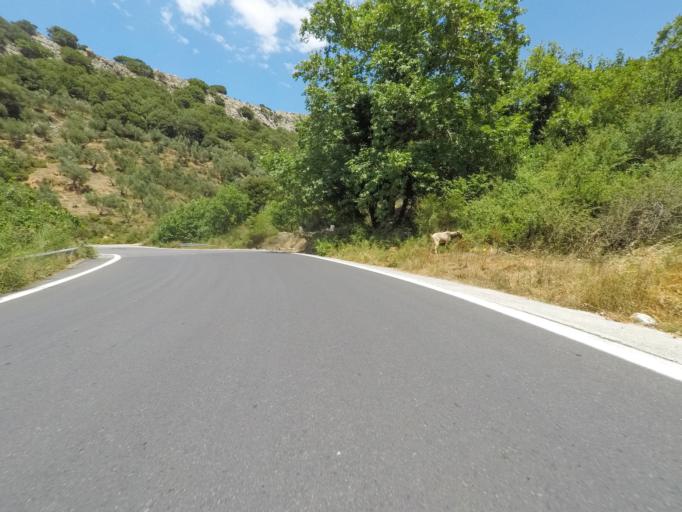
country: GR
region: Crete
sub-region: Nomos Irakleiou
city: Mokhos
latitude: 35.2300
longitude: 25.4633
